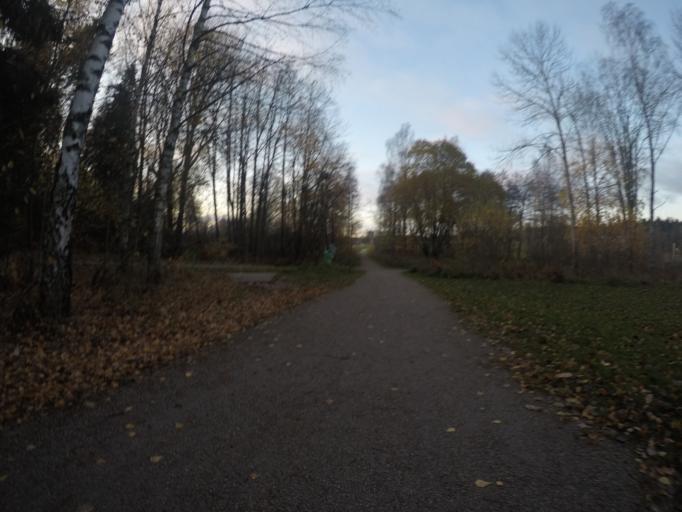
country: SE
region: Soedermanland
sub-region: Eskilstuna Kommun
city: Eskilstuna
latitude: 59.3479
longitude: 16.5100
